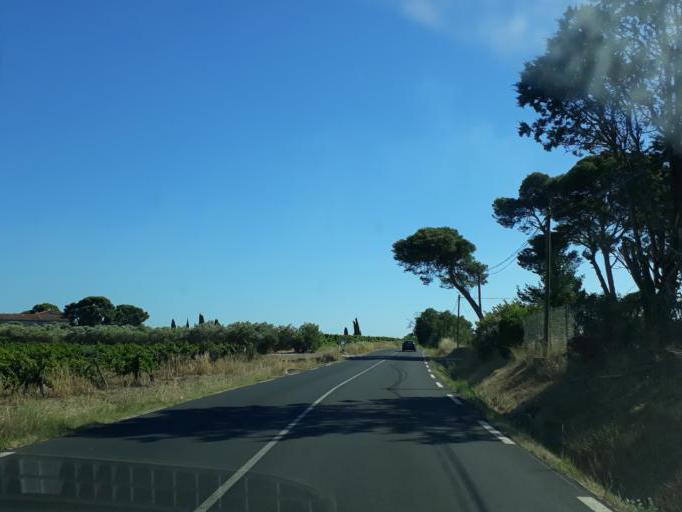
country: FR
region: Languedoc-Roussillon
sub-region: Departement de l'Herault
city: Agde
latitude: 43.3422
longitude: 3.4858
